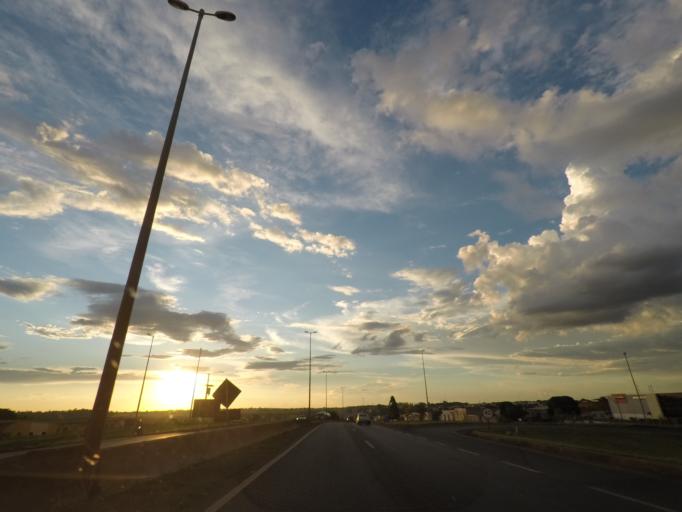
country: BR
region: Minas Gerais
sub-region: Uberaba
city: Uberaba
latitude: -19.7795
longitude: -47.9449
